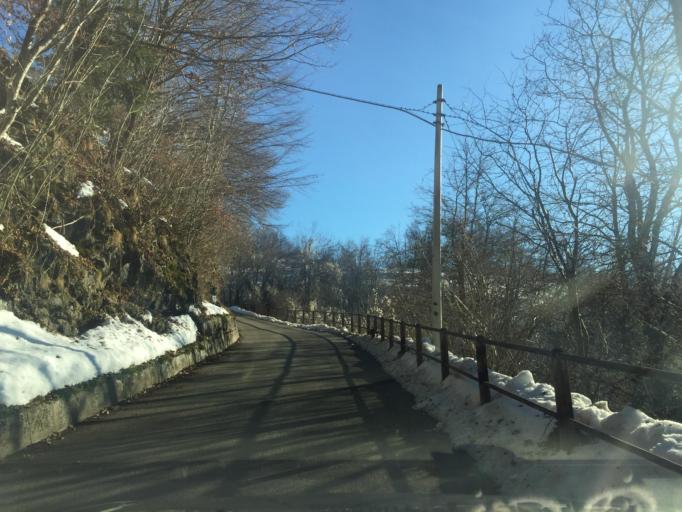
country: IT
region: Friuli Venezia Giulia
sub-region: Provincia di Udine
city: Lauco
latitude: 46.4418
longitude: 12.9569
